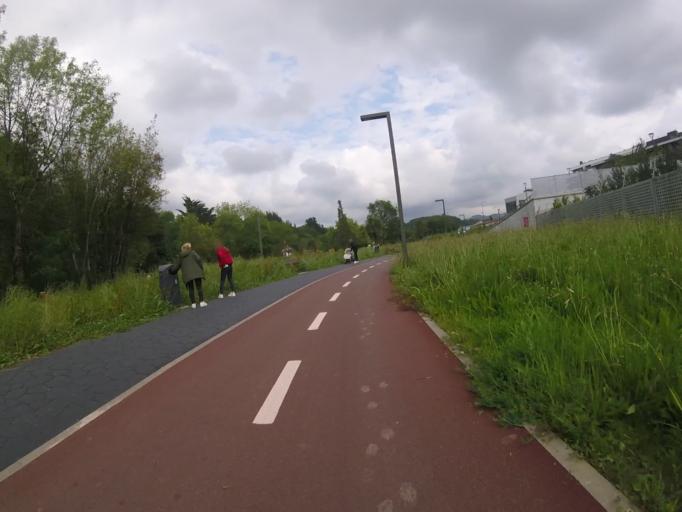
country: ES
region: Basque Country
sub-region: Provincia de Guipuzcoa
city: San Sebastian
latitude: 43.3054
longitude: -1.9585
